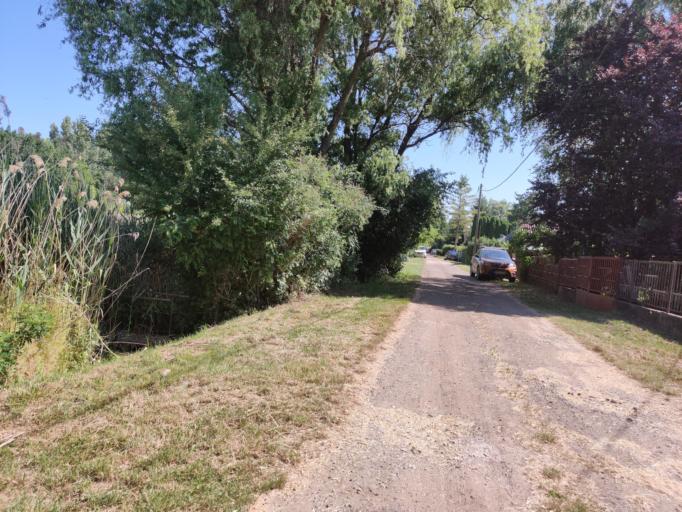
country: HU
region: Hajdu-Bihar
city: Balmazujvaros
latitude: 47.5902
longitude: 21.3676
